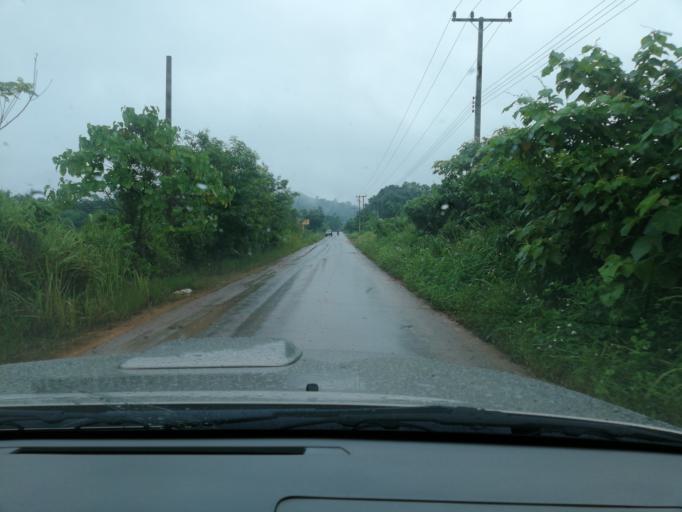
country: LA
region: Loungnamtha
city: Louang Namtha
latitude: 20.9803
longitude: 101.3865
